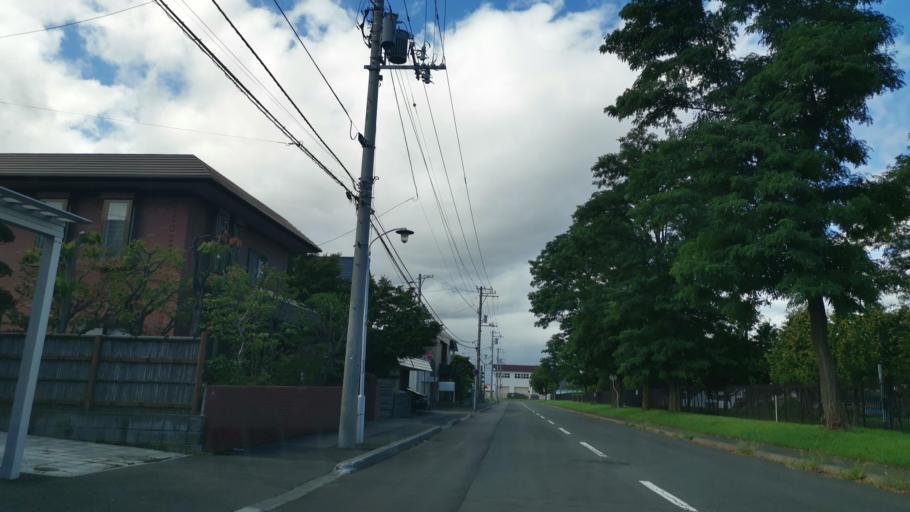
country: JP
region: Hokkaido
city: Sapporo
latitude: 42.9989
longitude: 141.3557
